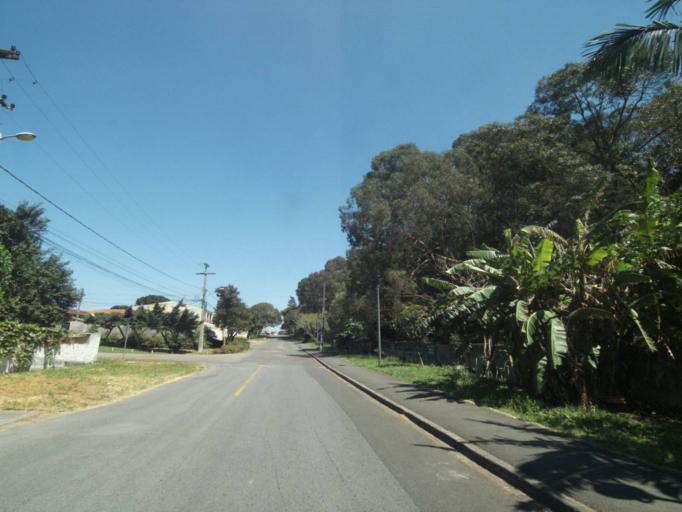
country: BR
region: Parana
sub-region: Sao Jose Dos Pinhais
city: Sao Jose dos Pinhais
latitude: -25.5089
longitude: -49.2404
